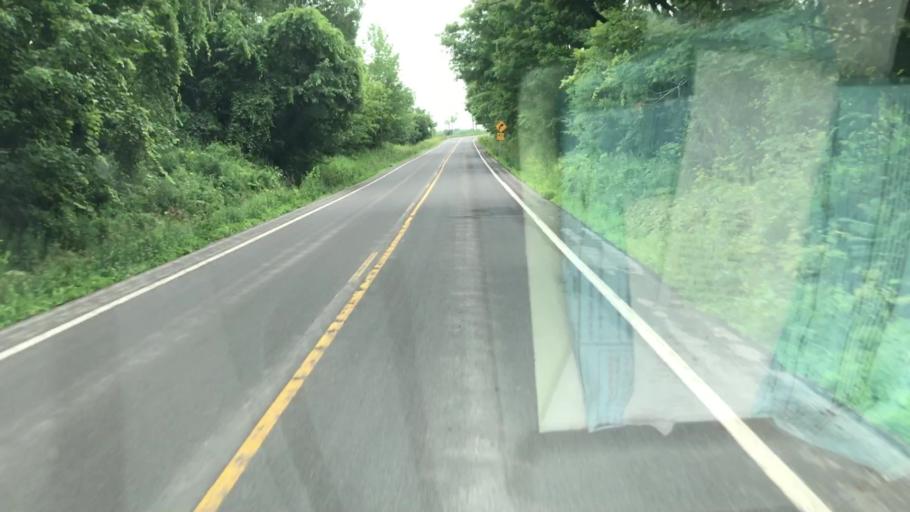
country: US
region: New York
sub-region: Onondaga County
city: Manlius
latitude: 42.9400
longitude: -75.9780
